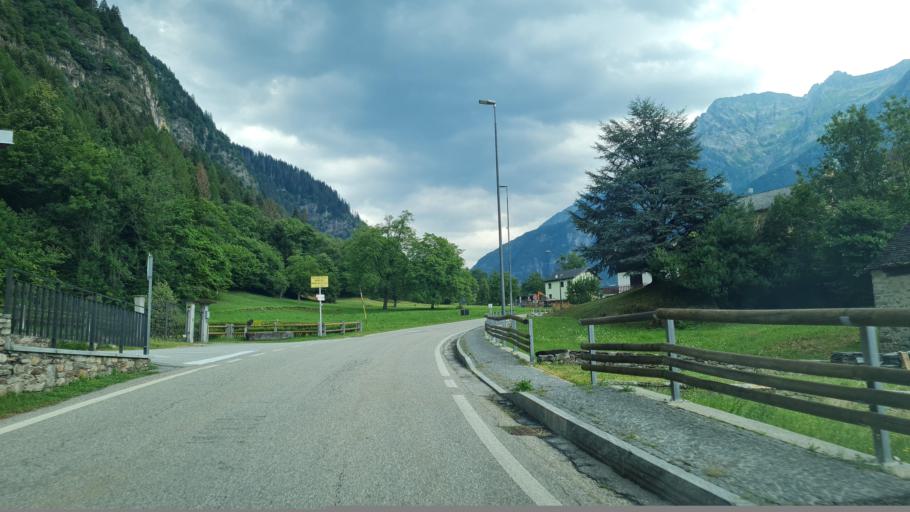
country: IT
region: Piedmont
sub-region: Provincia Verbano-Cusio-Ossola
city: Premia
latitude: 46.2667
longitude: 8.3334
